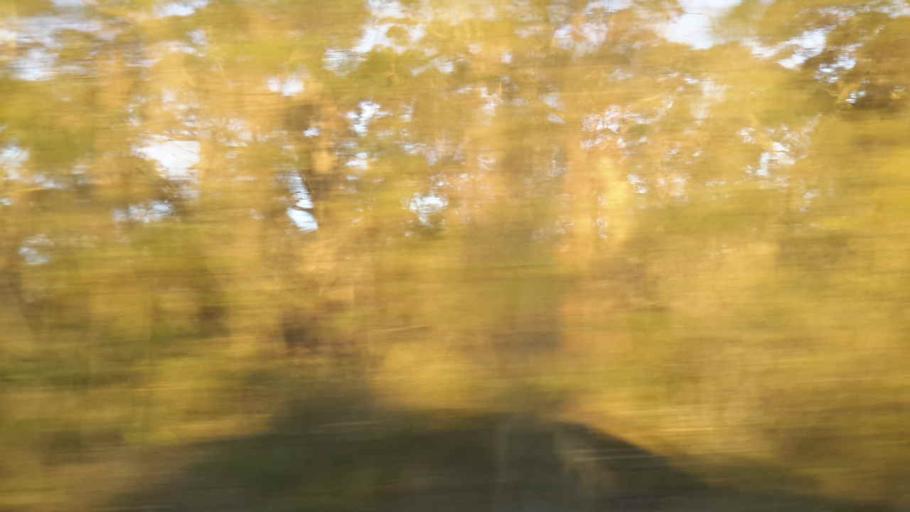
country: AU
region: New South Wales
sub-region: Wollongong
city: Mount Keira
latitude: -34.3922
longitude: 150.8411
